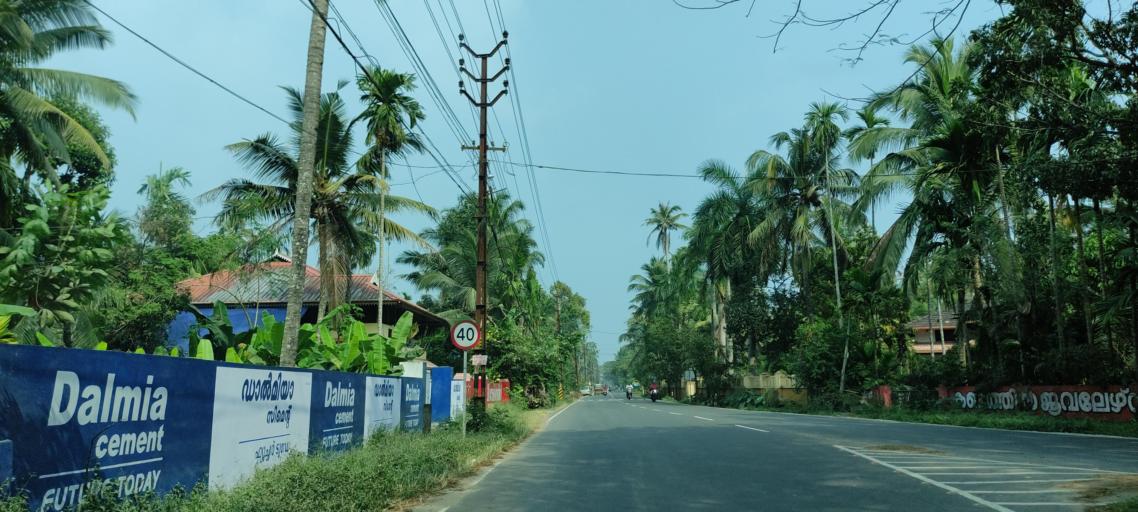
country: IN
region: Kerala
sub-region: Kottayam
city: Vaikam
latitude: 9.7706
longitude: 76.4186
